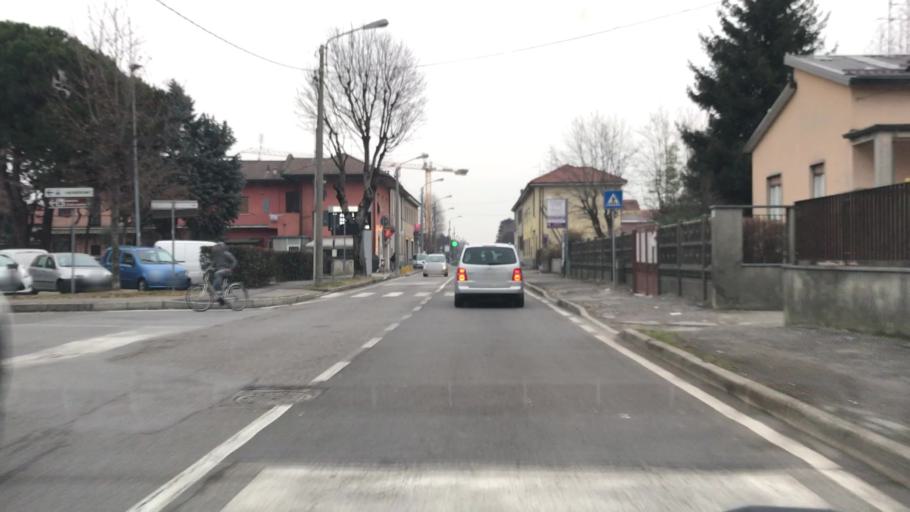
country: IT
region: Lombardy
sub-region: Provincia di Monza e Brianza
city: Seveso
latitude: 45.6424
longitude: 9.1445
